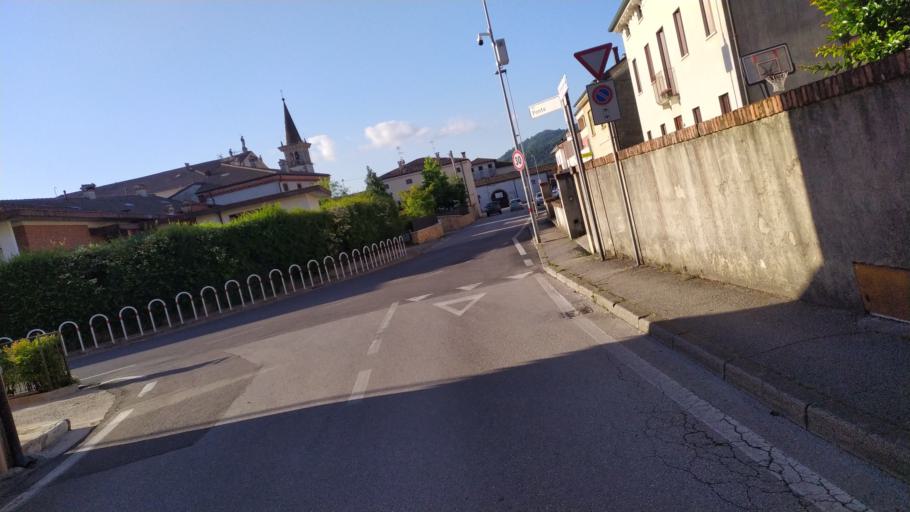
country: IT
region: Veneto
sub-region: Provincia di Vicenza
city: Malo
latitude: 45.6393
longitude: 11.4243
